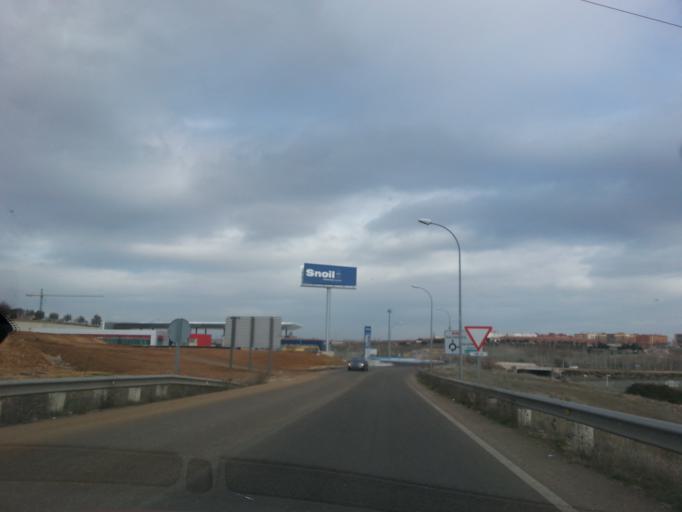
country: ES
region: Castille and Leon
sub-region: Provincia de Salamanca
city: Aldeatejada
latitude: 40.9411
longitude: -5.6816
